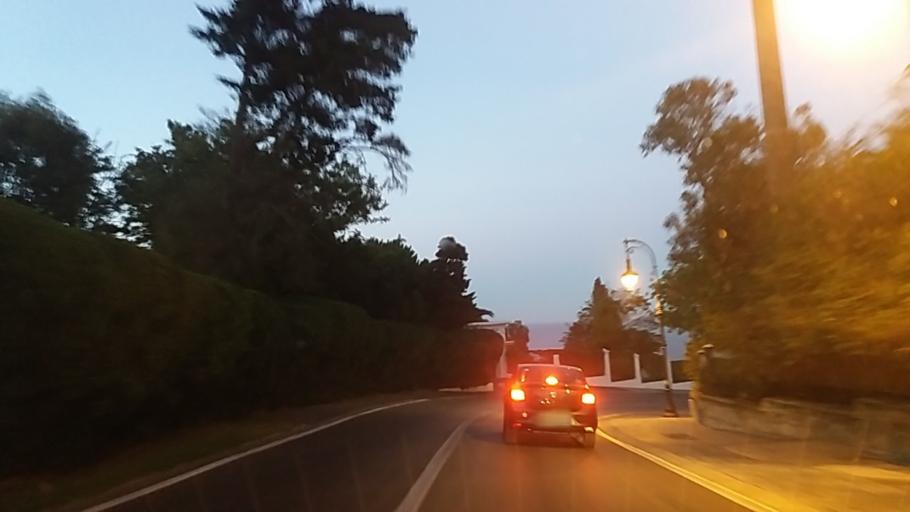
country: MA
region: Tanger-Tetouan
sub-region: Tanger-Assilah
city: Tangier
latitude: 35.7906
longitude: -5.8418
